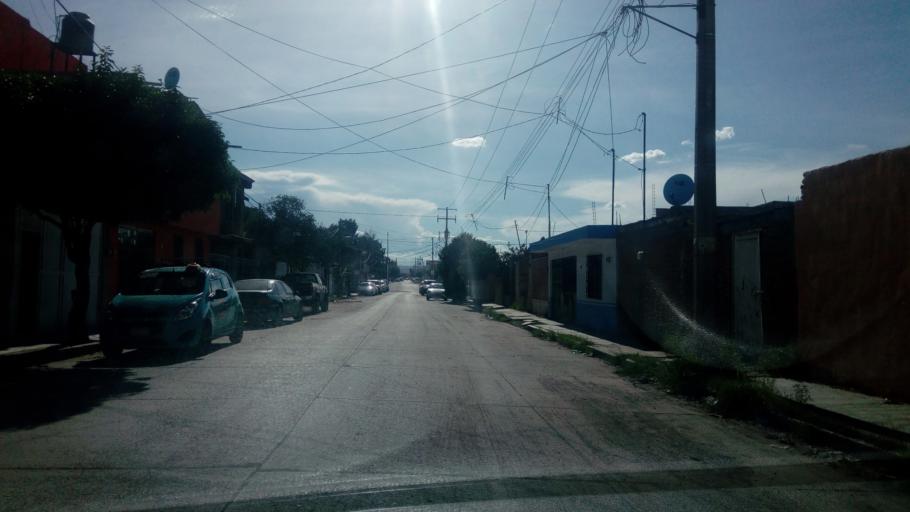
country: MX
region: Durango
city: Victoria de Durango
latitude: 24.0091
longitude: -104.6264
